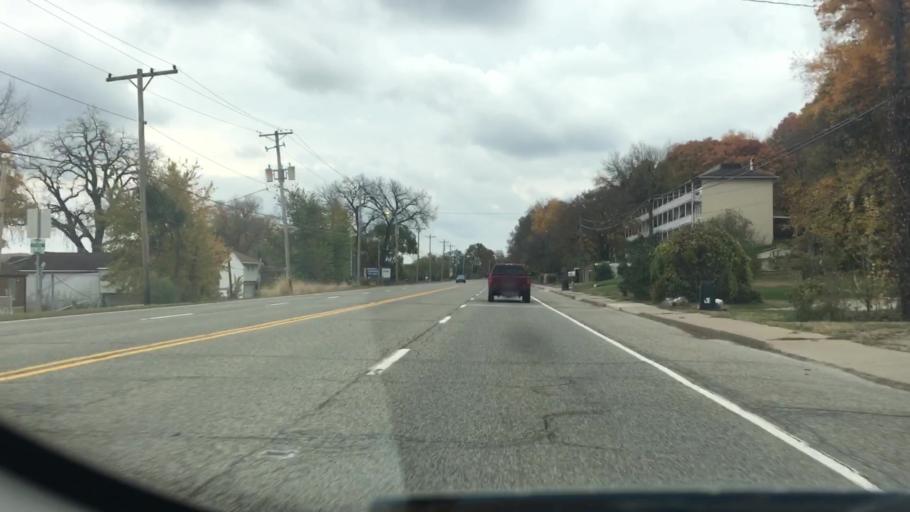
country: US
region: Illinois
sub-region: Peoria County
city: Peoria Heights
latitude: 40.7458
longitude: -89.5567
